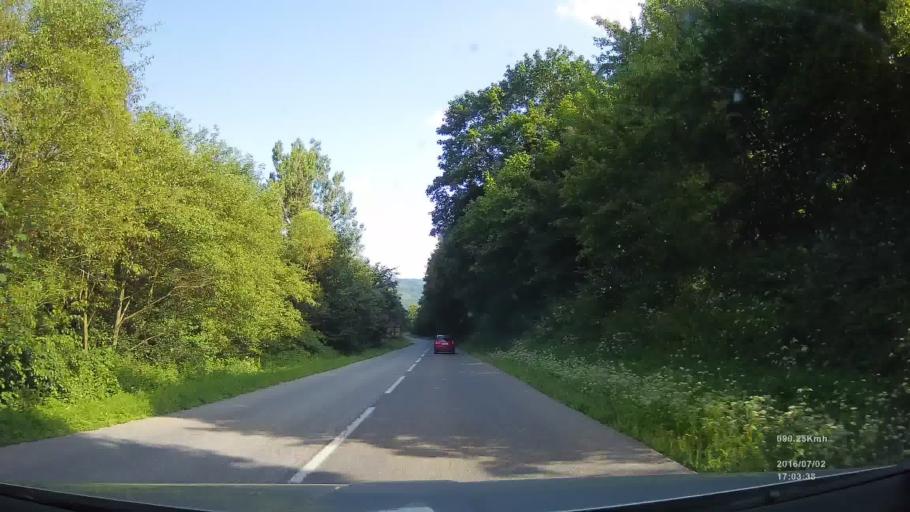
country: SK
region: Kosicky
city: Gelnica
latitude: 48.8709
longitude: 21.0027
